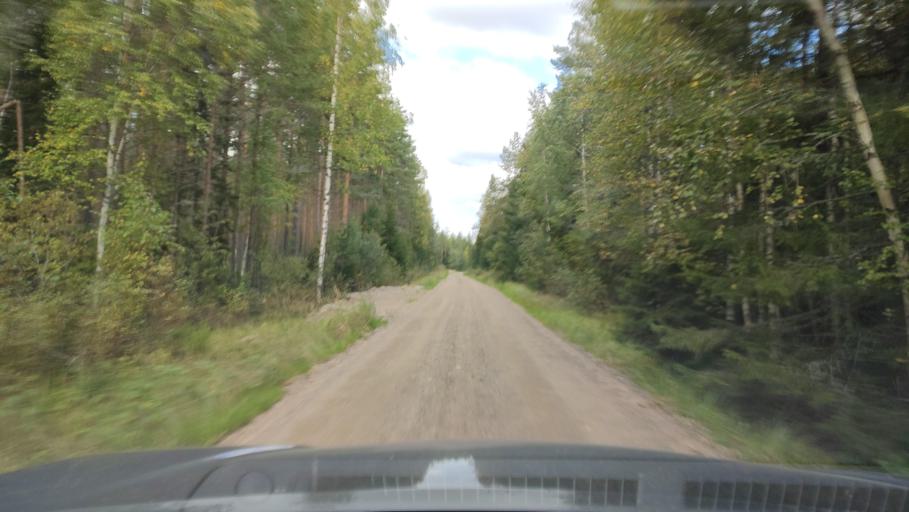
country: FI
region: Southern Ostrobothnia
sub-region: Suupohja
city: Karijoki
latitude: 62.2055
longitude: 21.6152
